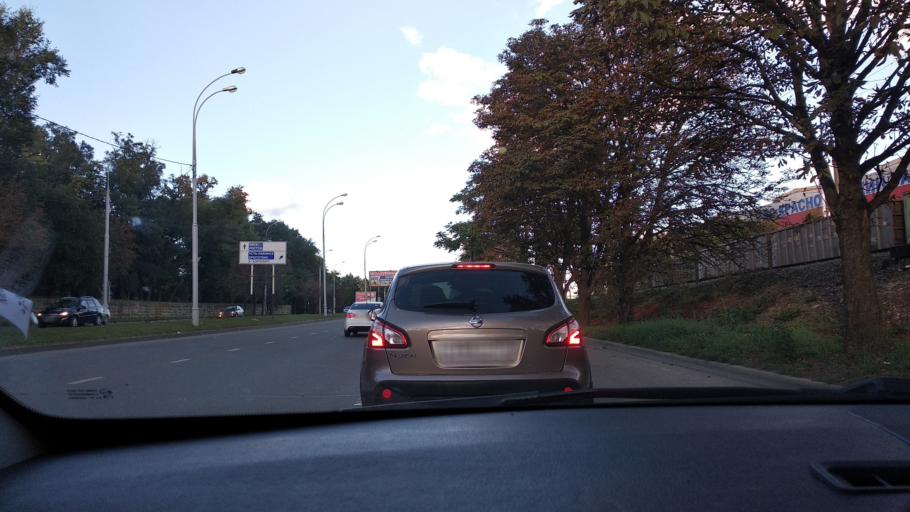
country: RU
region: Krasnodarskiy
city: Krasnodar
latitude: 45.0108
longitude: 38.9722
